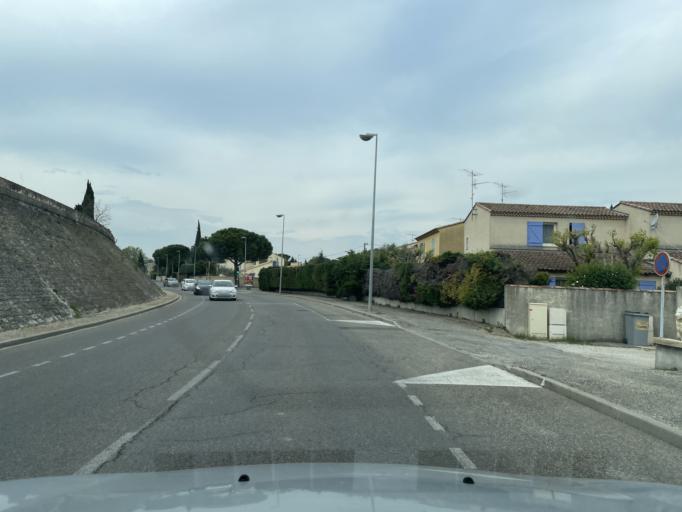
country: FR
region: Provence-Alpes-Cote d'Azur
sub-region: Departement des Bouches-du-Rhone
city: Tarascon
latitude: 43.8112
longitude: 4.6625
